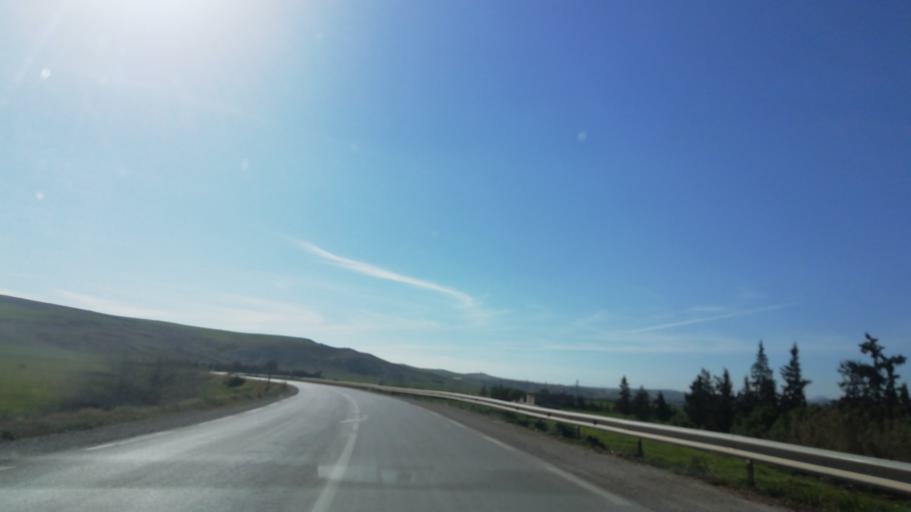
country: DZ
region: Mascara
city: Oued el Abtal
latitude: 35.4585
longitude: 0.7481
